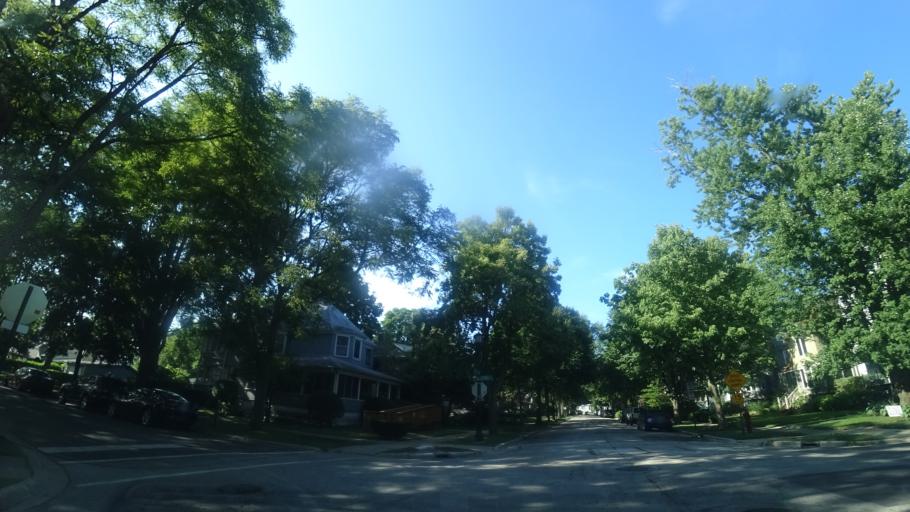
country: US
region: Illinois
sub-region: Cook County
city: Evanston
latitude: 42.0502
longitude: -87.6920
